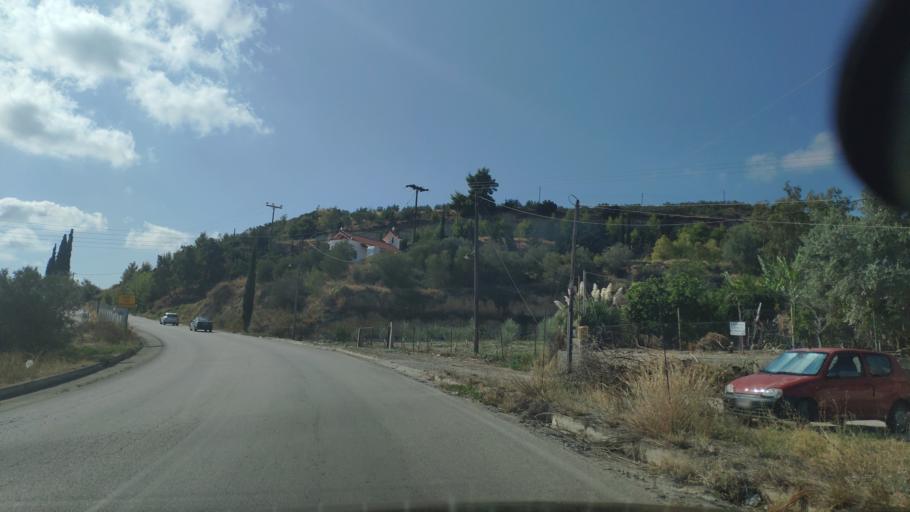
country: GR
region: Peloponnese
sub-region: Nomos Korinthias
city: Moulki
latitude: 38.0004
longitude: 22.7174
